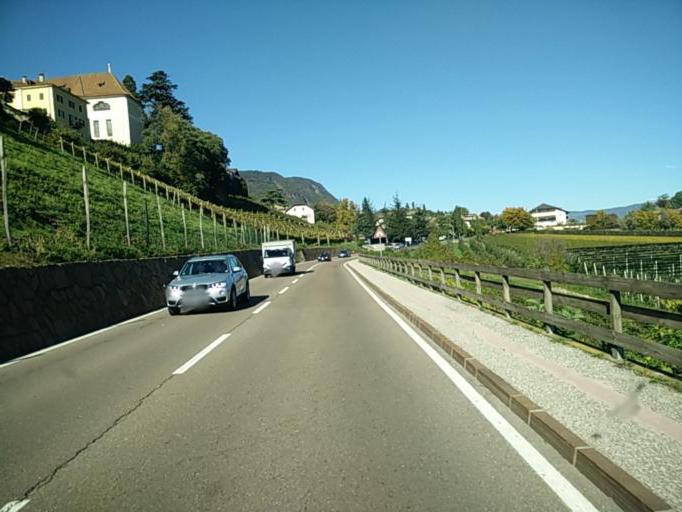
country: IT
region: Trentino-Alto Adige
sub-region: Bolzano
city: Caldaro sulla Strada del Vino
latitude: 46.4120
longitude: 11.2479
